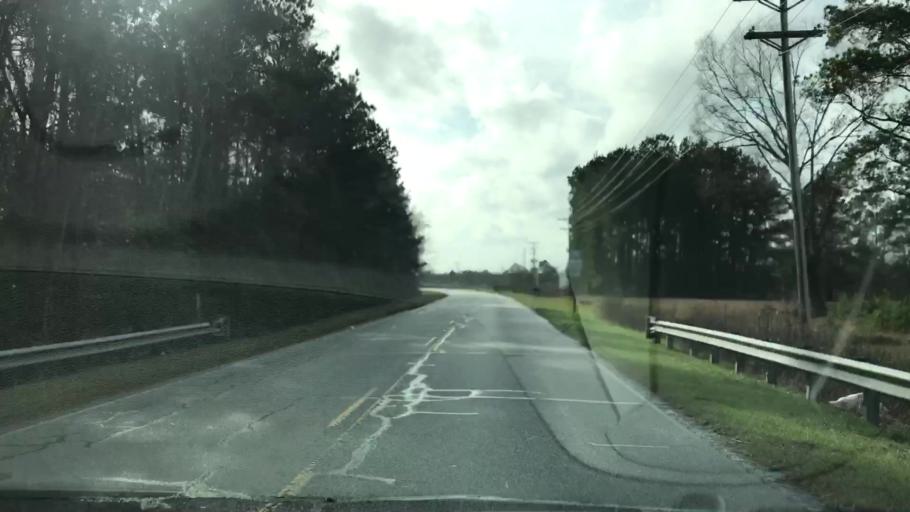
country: US
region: South Carolina
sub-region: Williamsburg County
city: Andrews
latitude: 33.4972
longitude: -79.5375
